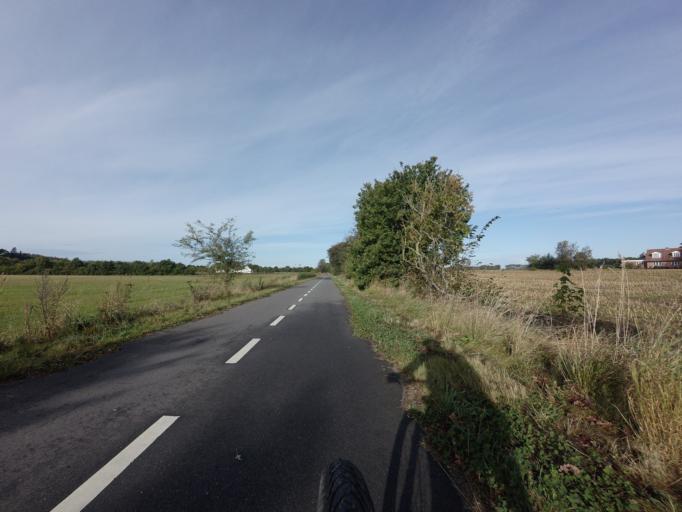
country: DK
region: Central Jutland
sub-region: Viborg Kommune
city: Viborg
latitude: 56.4248
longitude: 9.4274
